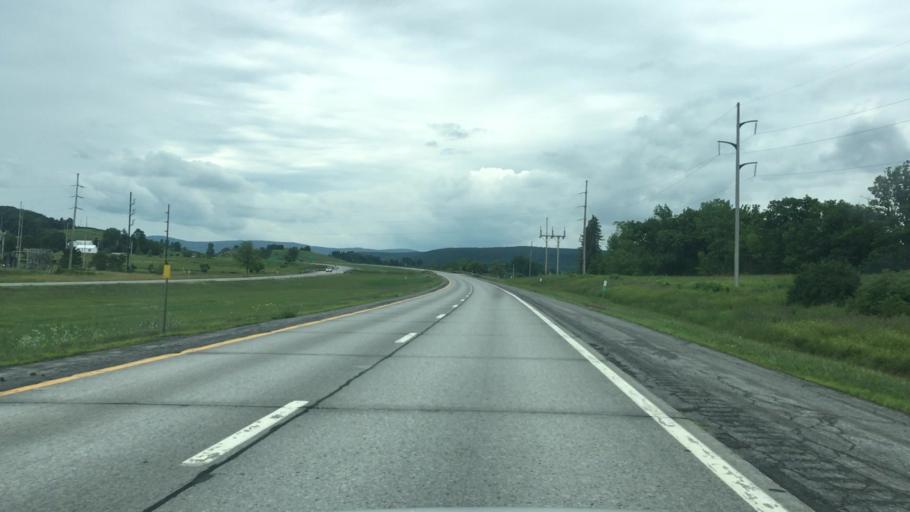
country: US
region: New York
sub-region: Schoharie County
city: Cobleskill
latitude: 42.6729
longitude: -74.4778
